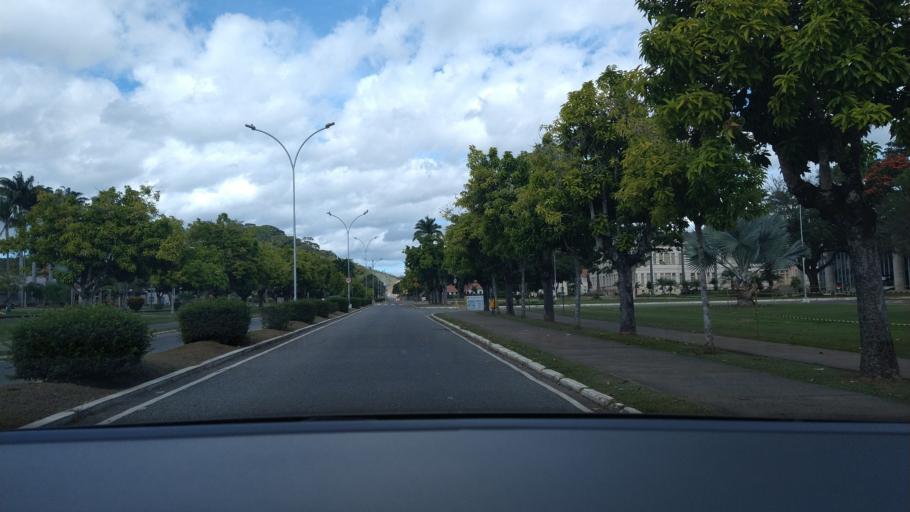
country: BR
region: Minas Gerais
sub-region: Vicosa
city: Vicosa
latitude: -20.7604
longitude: -42.8701
